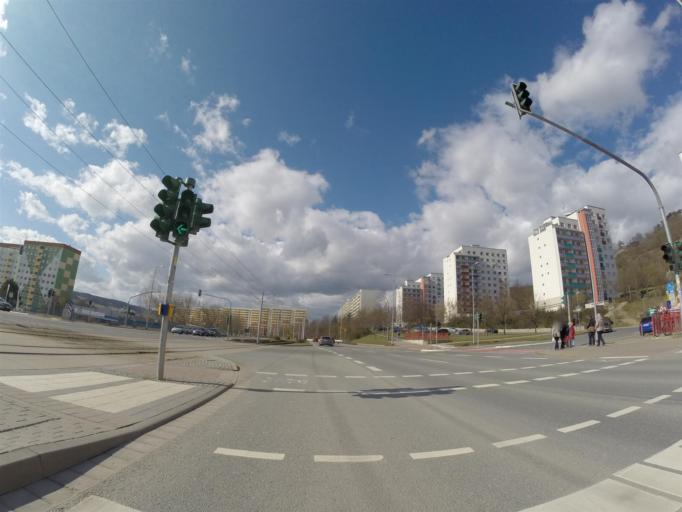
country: DE
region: Thuringia
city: Sulza
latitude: 50.8869
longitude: 11.6163
